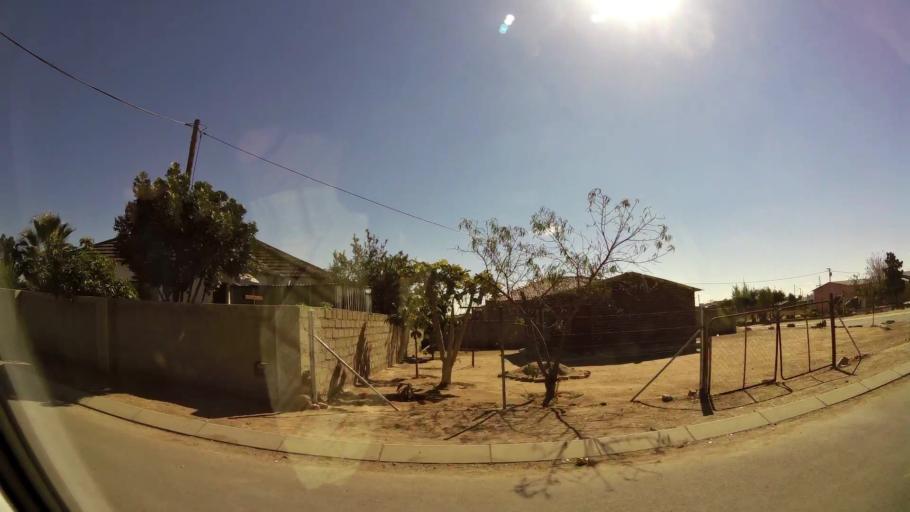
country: ZA
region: Limpopo
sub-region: Capricorn District Municipality
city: Polokwane
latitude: -23.8492
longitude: 29.4110
